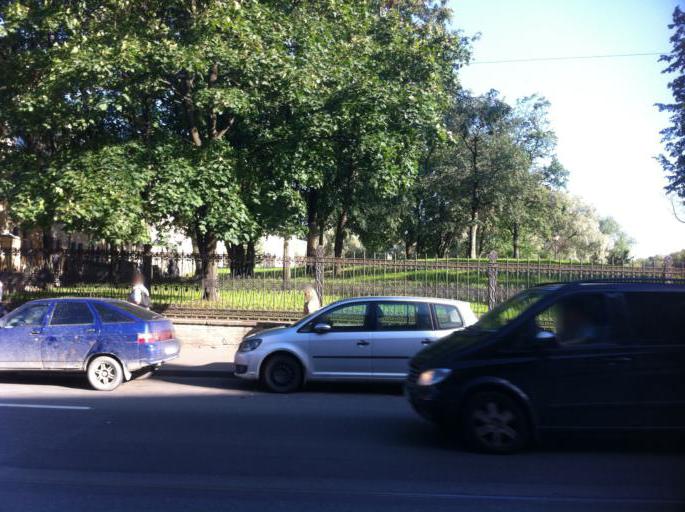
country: RU
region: St.-Petersburg
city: Saint Petersburg
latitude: 59.9246
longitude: 30.3127
